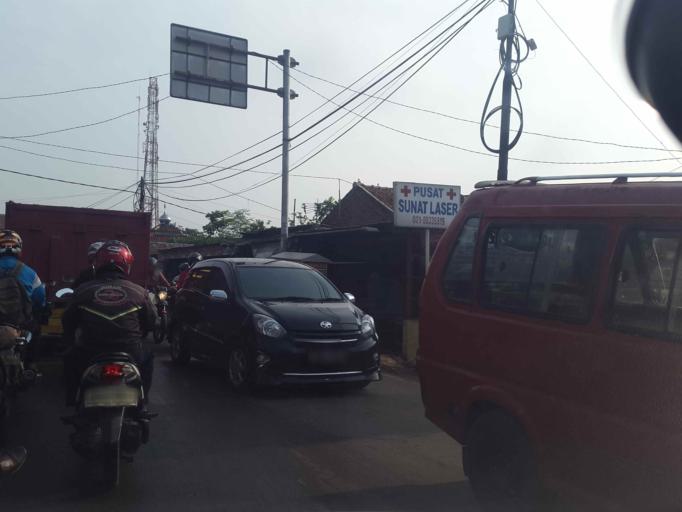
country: ID
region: West Java
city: Bekasi
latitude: -6.2714
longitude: 107.0473
